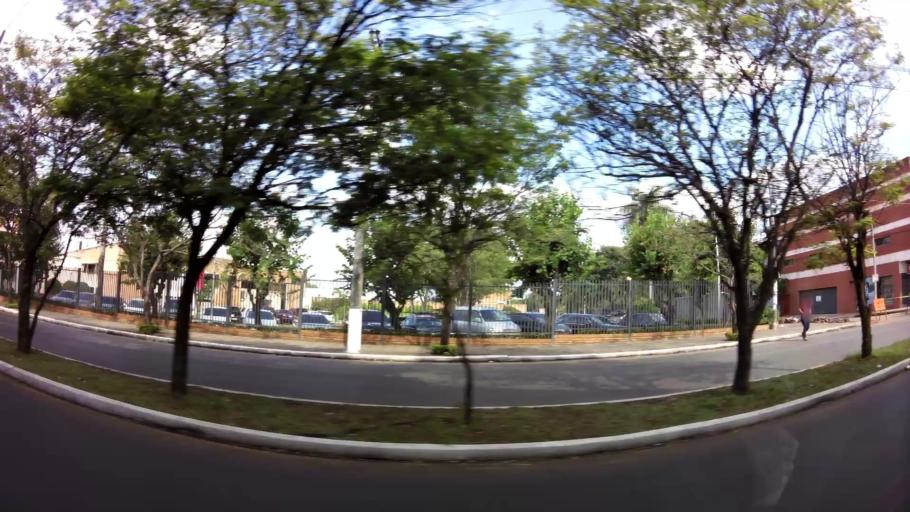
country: PY
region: Central
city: Fernando de la Mora
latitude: -25.3385
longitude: -57.5379
